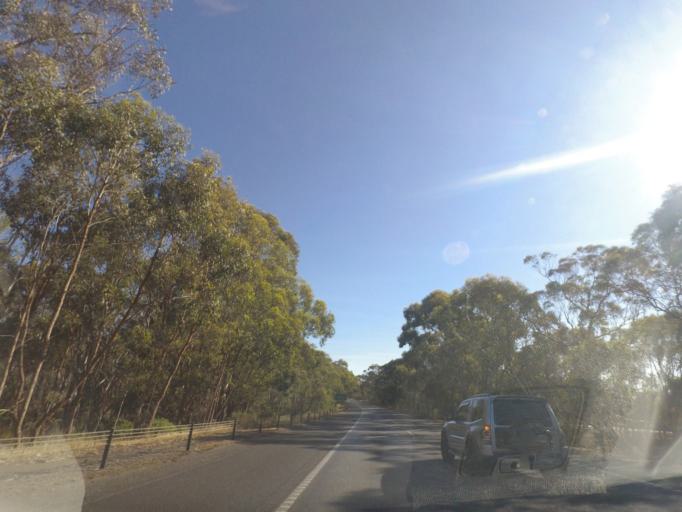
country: AU
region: Victoria
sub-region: Murrindindi
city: Kinglake West
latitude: -37.1767
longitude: 145.0717
